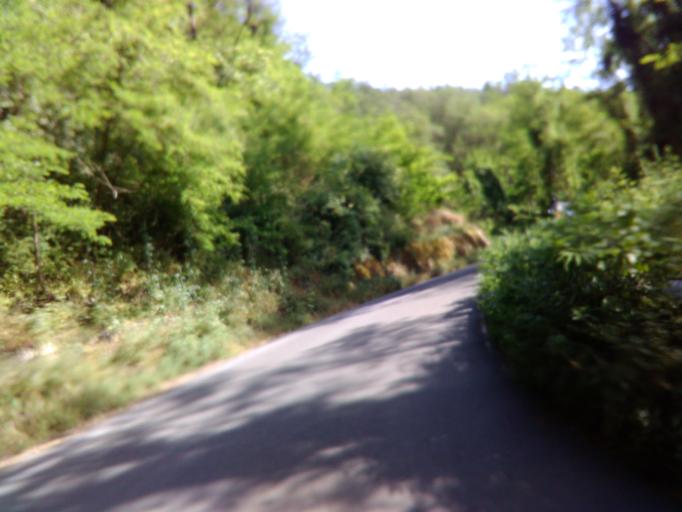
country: IT
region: Tuscany
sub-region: Provincia di Massa-Carrara
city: Fosdinovo
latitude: 44.1185
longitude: 10.0650
